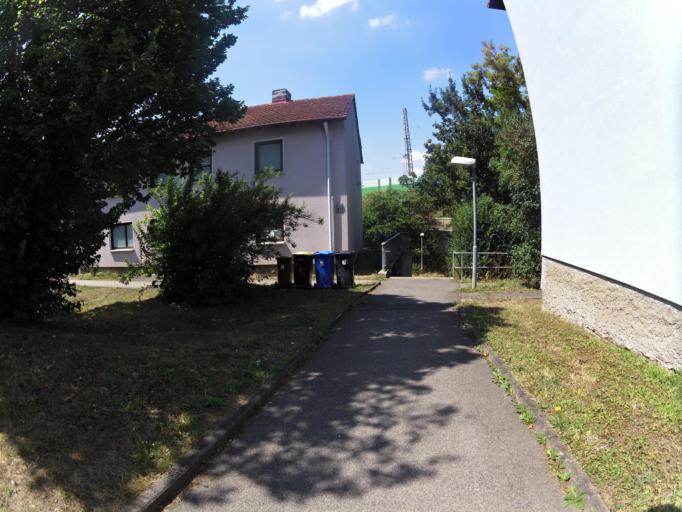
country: DE
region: Bavaria
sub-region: Regierungsbezirk Unterfranken
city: Frickenhausen
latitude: 49.6637
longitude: 10.0836
